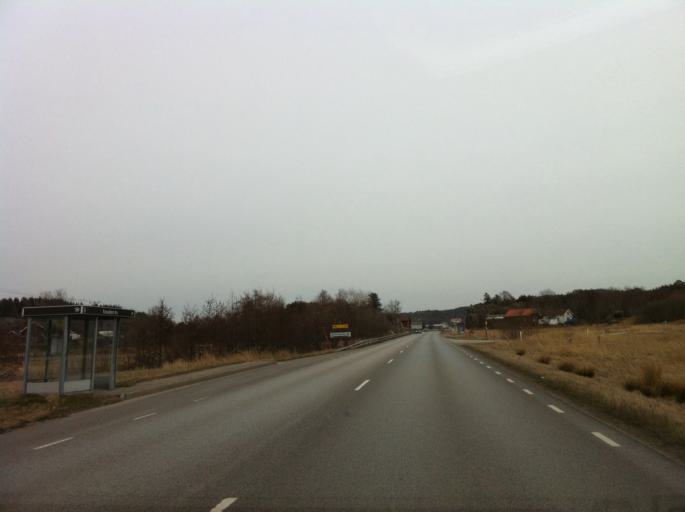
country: SE
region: Vaestra Goetaland
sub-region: Tjorns Kommun
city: Skaerhamn
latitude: 57.9981
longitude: 11.5949
